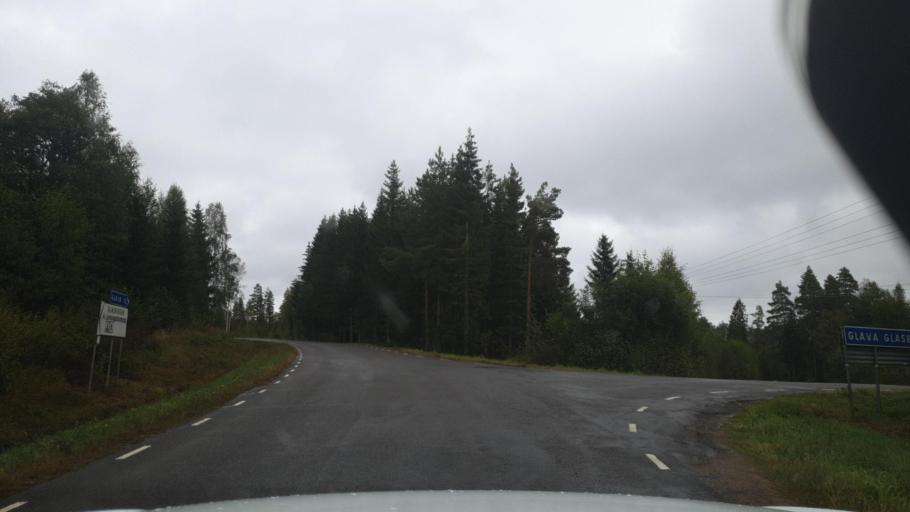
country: SE
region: Vaermland
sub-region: Arvika Kommun
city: Arvika
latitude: 59.5341
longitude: 12.3952
